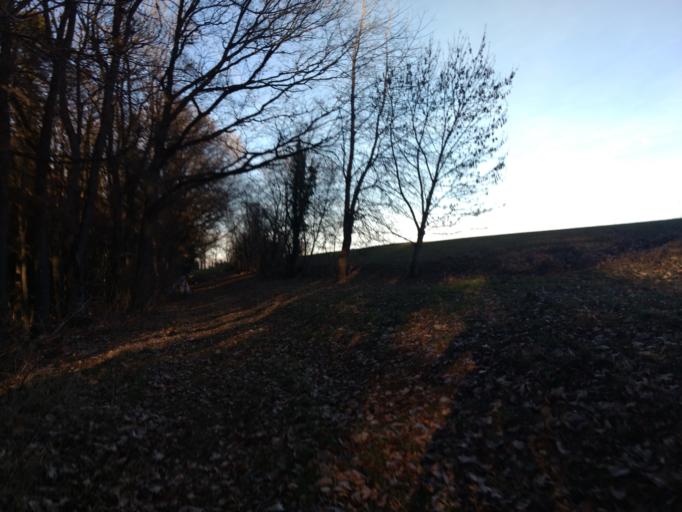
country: DE
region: Baden-Wuerttemberg
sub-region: Regierungsbezirk Stuttgart
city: Waschenbeuren
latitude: 48.7418
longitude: 9.6853
